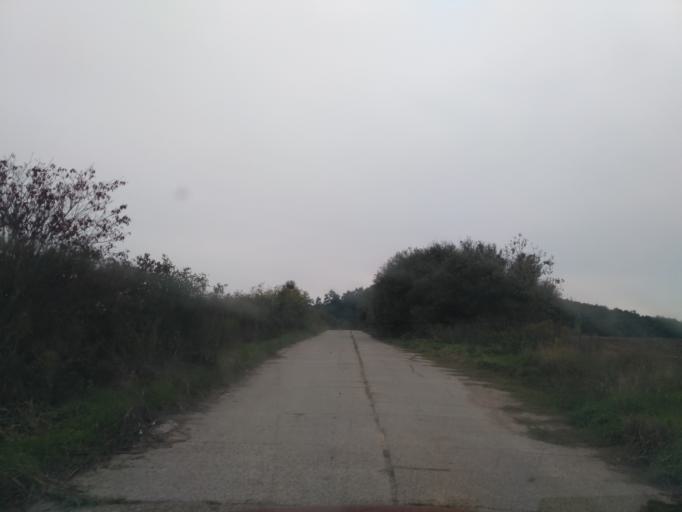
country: SK
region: Kosicky
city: Kosice
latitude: 48.8029
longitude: 21.2744
